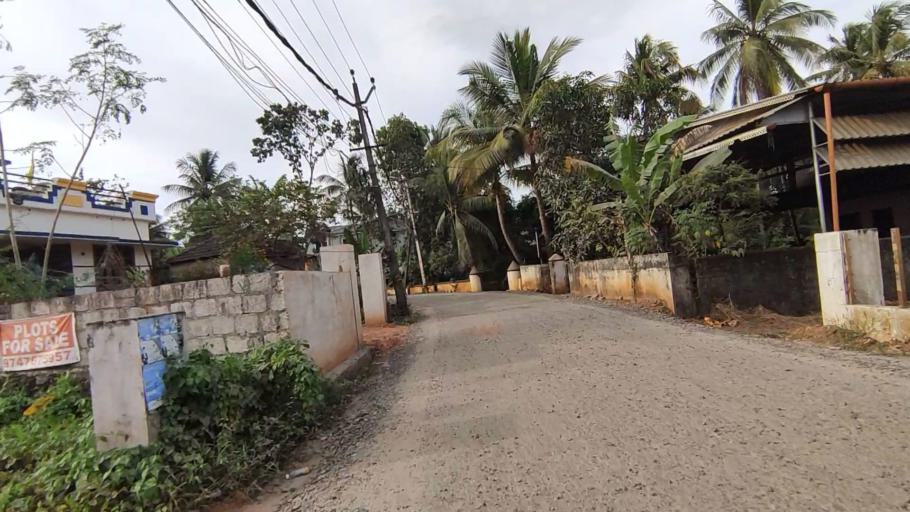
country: IN
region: Kerala
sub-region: Kottayam
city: Kottayam
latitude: 9.5862
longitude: 76.4923
